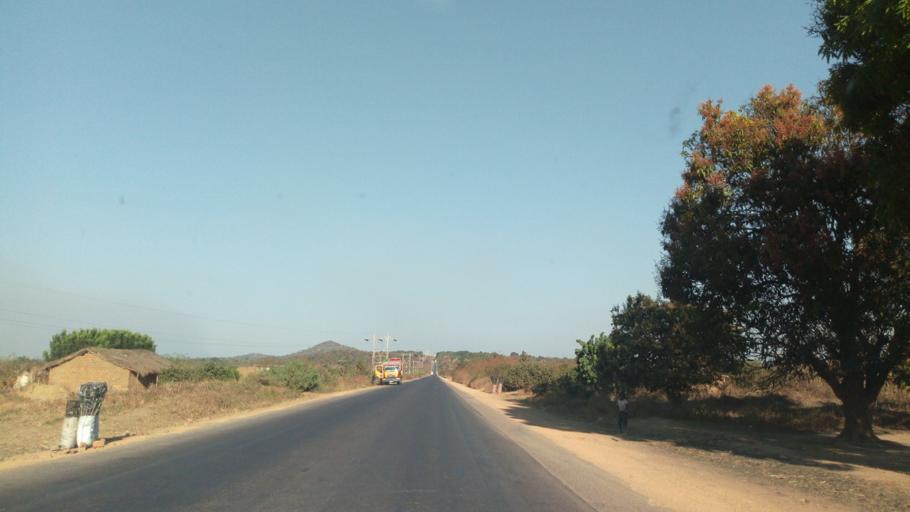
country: CD
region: Katanga
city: Likasi
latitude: -11.0502
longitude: 26.9572
